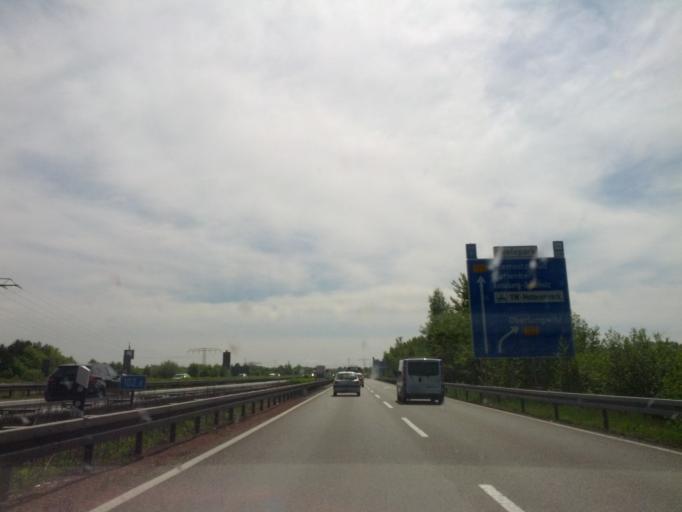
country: DE
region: Saxony
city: Neukirchen
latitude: 50.8122
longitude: 12.8586
